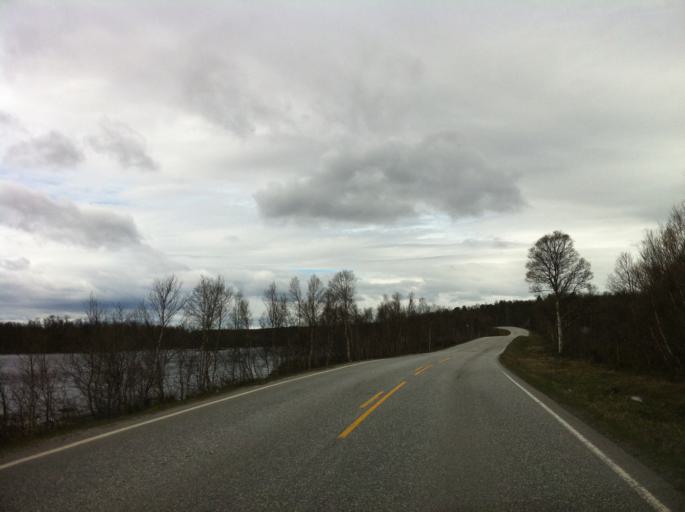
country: NO
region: Sor-Trondelag
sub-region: Roros
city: Roros
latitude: 62.5996
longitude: 11.4947
